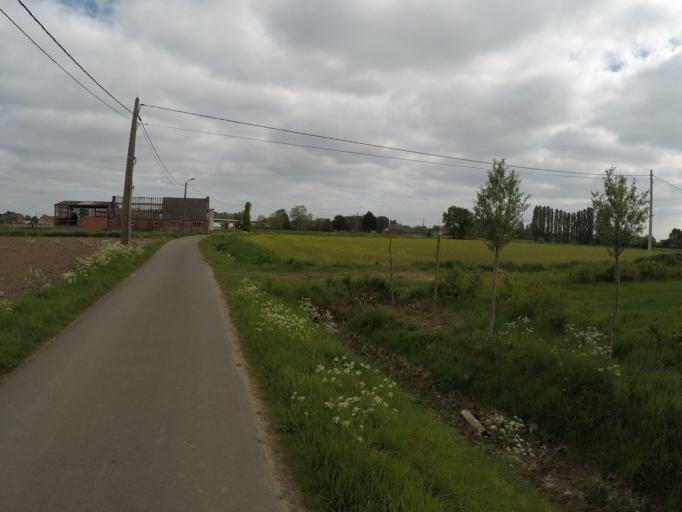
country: BE
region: Flanders
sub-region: Provincie Antwerpen
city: Ranst
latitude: 51.1787
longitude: 4.5516
